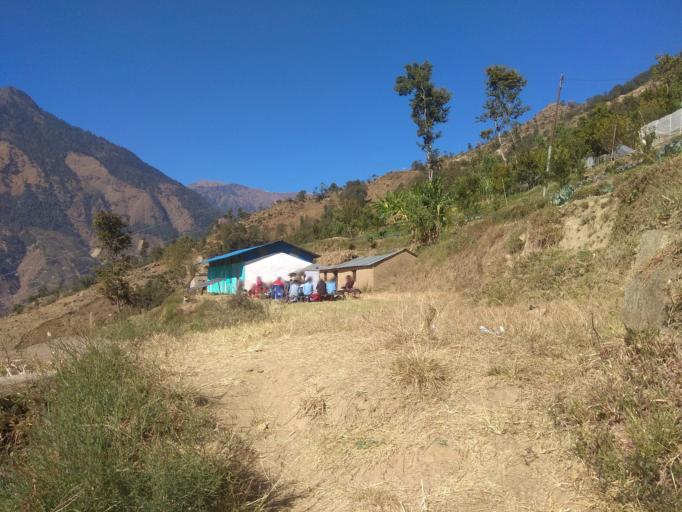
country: NP
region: Far Western
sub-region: Seti Zone
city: Achham
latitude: 29.2535
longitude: 81.6226
